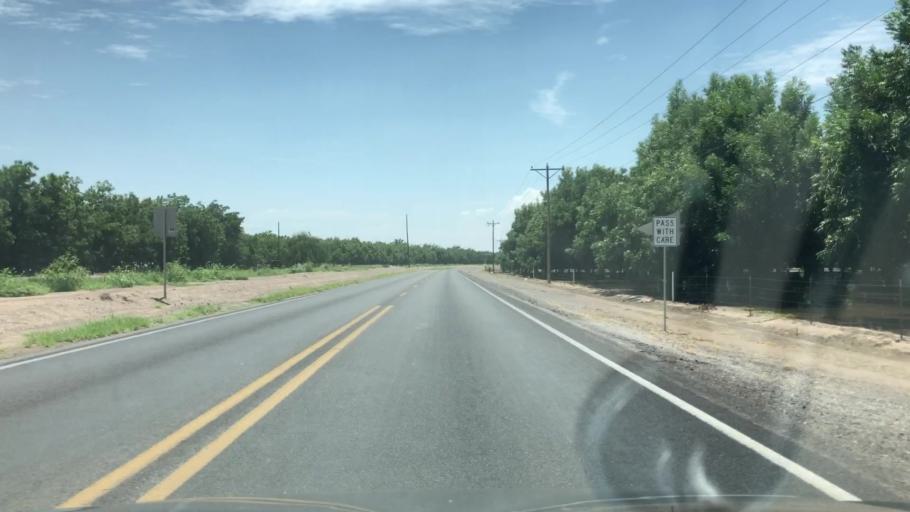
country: US
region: New Mexico
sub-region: Dona Ana County
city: La Union
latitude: 31.9937
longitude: -106.6529
